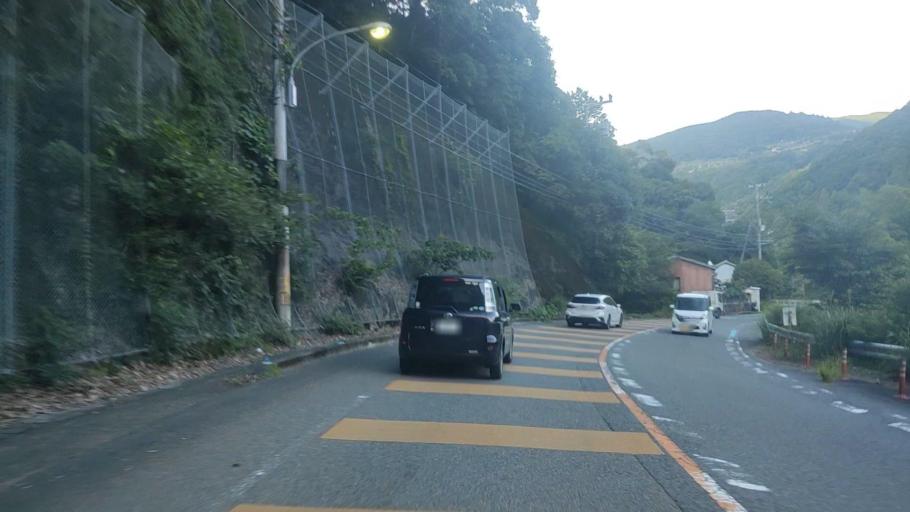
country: JP
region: Wakayama
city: Tanabe
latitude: 33.7985
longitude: 135.5207
